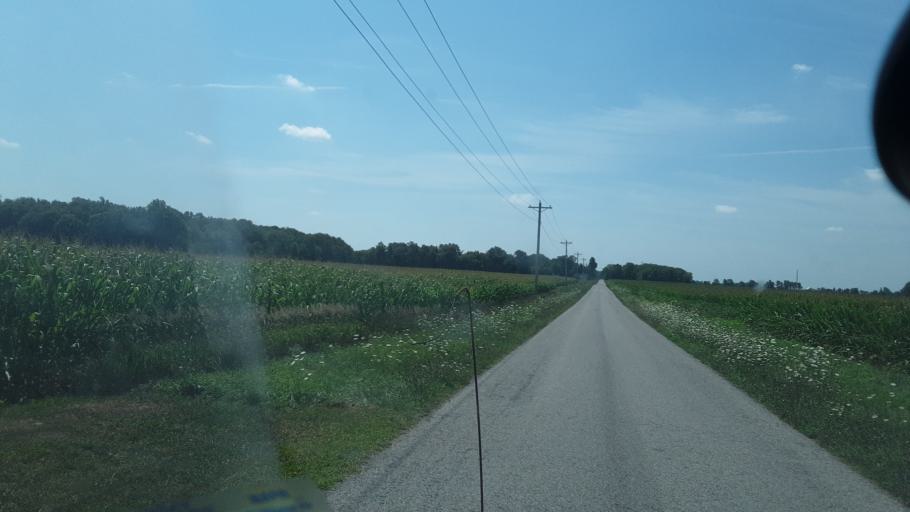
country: US
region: Ohio
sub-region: Hancock County
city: Findlay
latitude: 40.9740
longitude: -83.5553
